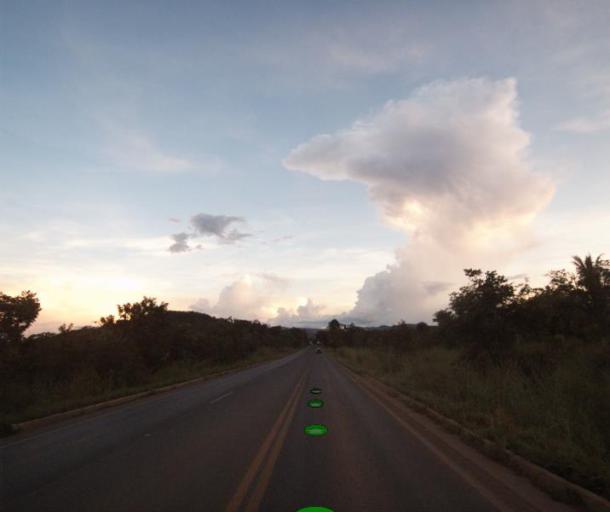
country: BR
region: Goias
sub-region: Uruacu
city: Uruacu
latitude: -14.4846
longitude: -49.1536
